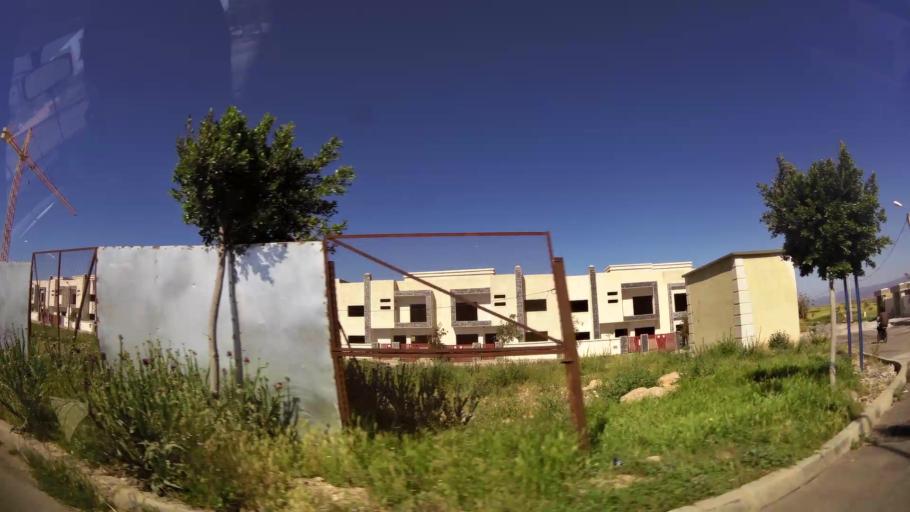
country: MA
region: Oriental
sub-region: Oujda-Angad
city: Oujda
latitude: 34.7331
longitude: -1.9181
